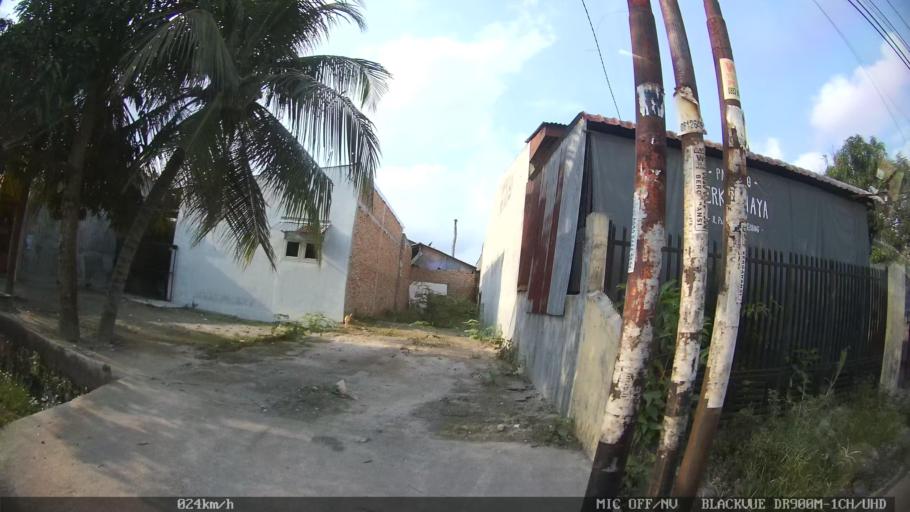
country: ID
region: North Sumatra
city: Medan
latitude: 3.5852
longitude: 98.7531
